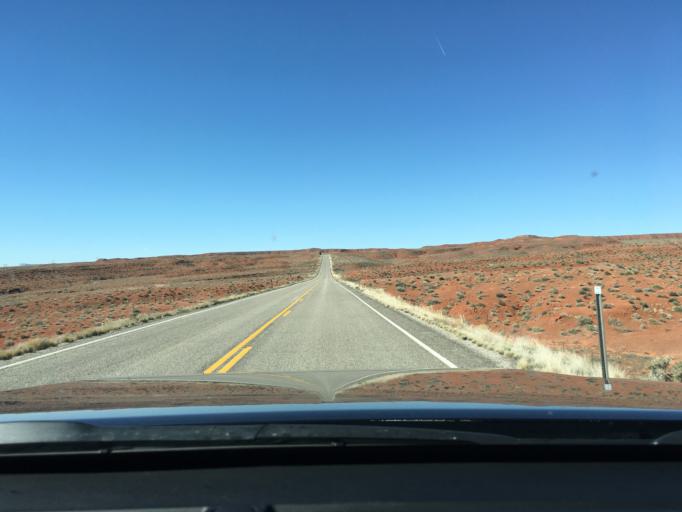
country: US
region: Utah
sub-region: San Juan County
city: Blanding
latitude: 37.2096
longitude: -109.8503
